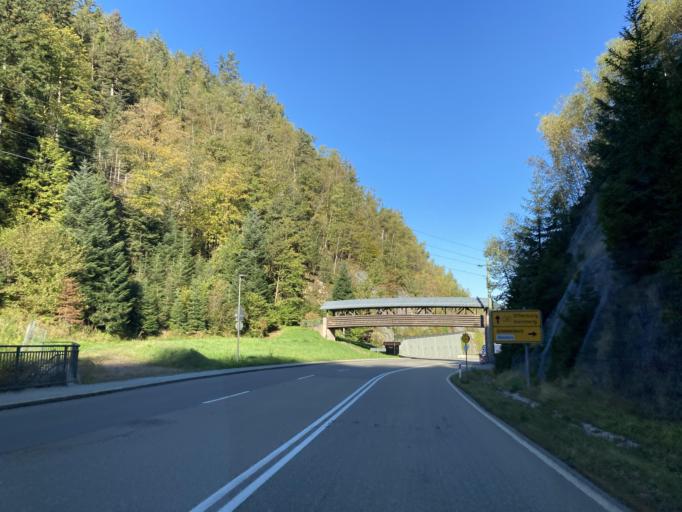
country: DE
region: Baden-Wuerttemberg
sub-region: Freiburg Region
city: Triberg im Schwarzwald
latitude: 48.1583
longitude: 8.2398
